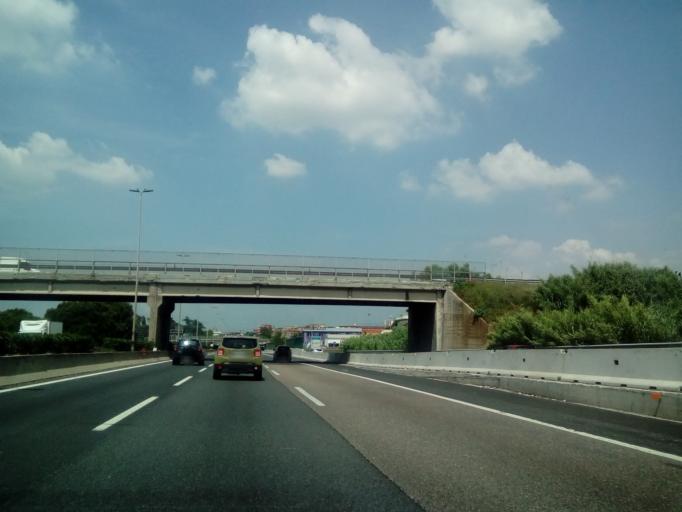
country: IT
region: Latium
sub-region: Citta metropolitana di Roma Capitale
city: Setteville
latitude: 41.8820
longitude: 12.6109
